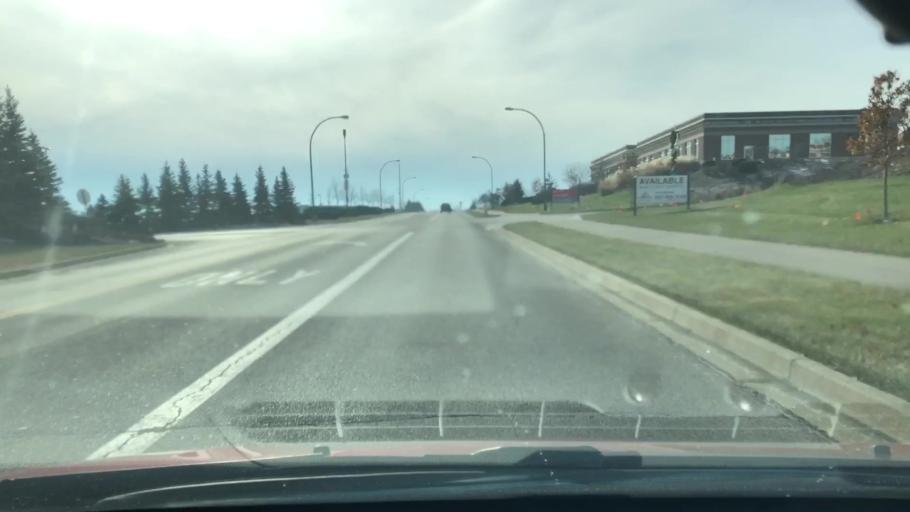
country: US
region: Ohio
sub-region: Greene County
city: Wright-Patterson AFB
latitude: 39.7686
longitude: -84.0596
